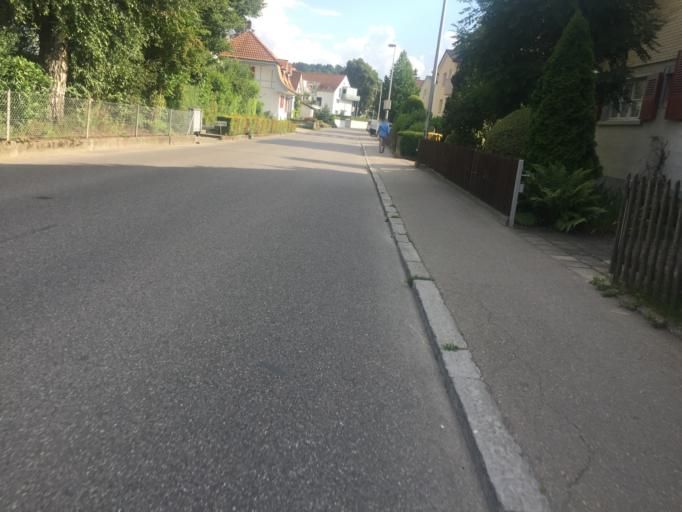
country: CH
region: Bern
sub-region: Bern-Mittelland District
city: Bolligen
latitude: 46.9607
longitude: 7.4954
